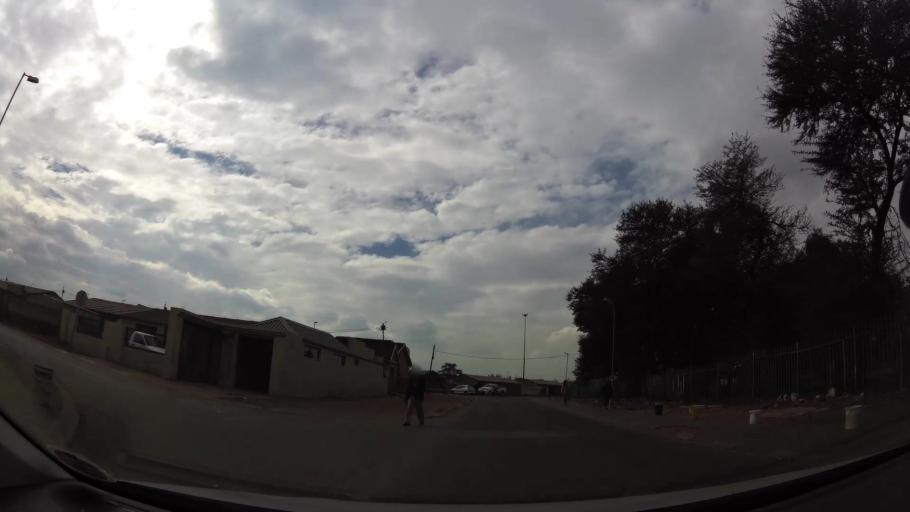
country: ZA
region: Gauteng
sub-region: City of Johannesburg Metropolitan Municipality
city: Soweto
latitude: -26.2701
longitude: 27.8553
